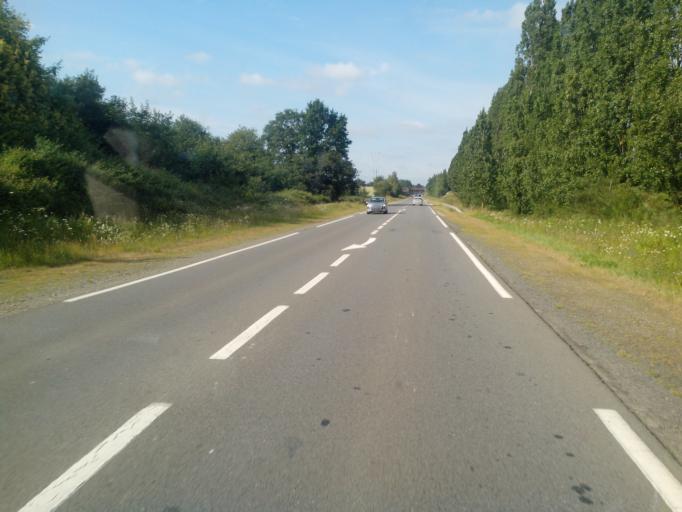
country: FR
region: Brittany
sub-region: Departement d'Ille-et-Vilaine
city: Le Rheu
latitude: 48.0939
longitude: -1.7907
